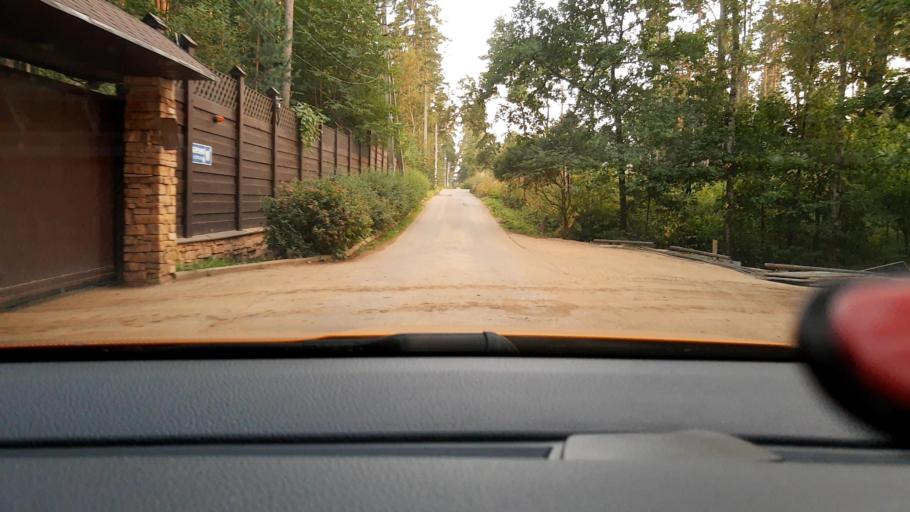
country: RU
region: Moscow
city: Novo-Peredelkino
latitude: 55.6688
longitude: 37.3426
